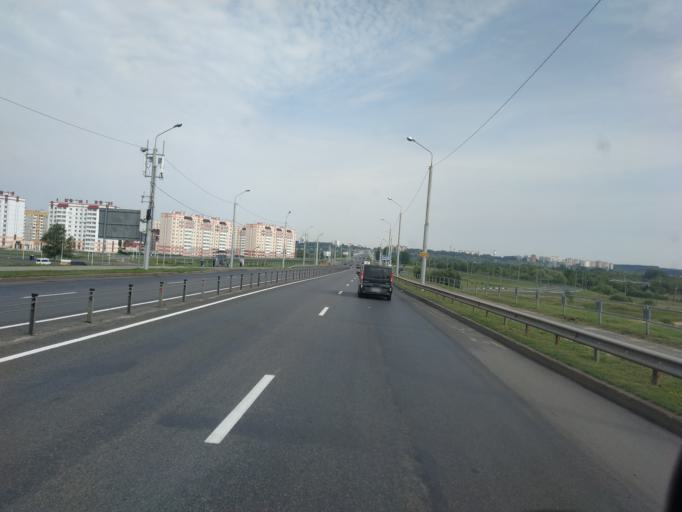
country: BY
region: Mogilev
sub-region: Mahilyowski Rayon
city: Veyno
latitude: 53.8807
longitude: 30.3824
